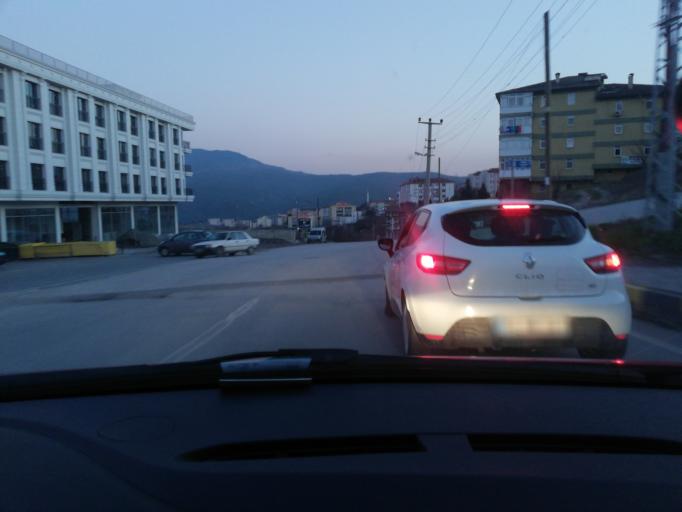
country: TR
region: Karabuk
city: Safranbolu
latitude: 41.2282
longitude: 32.6691
